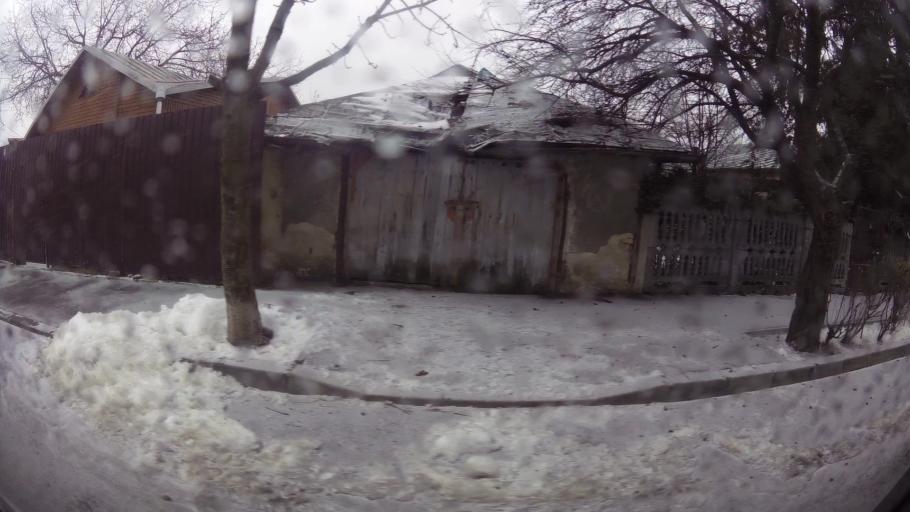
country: RO
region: Prahova
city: Ploiesti
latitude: 44.9561
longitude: 26.0418
